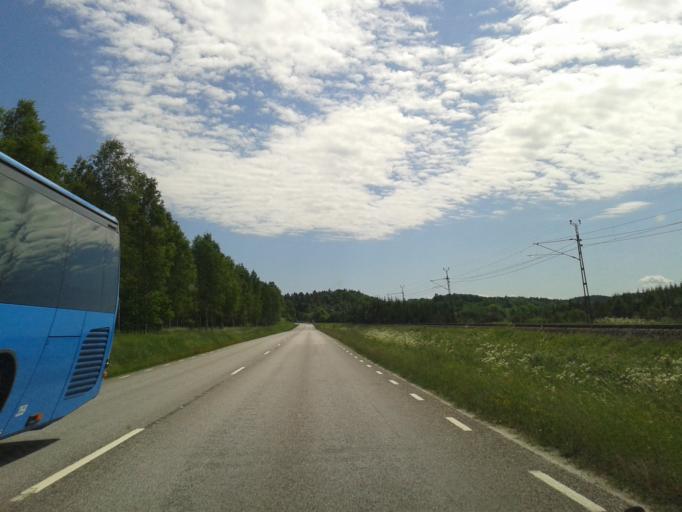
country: SE
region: Vaestra Goetaland
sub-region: Uddevalla Kommun
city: Ljungskile
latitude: 58.2684
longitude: 11.8942
